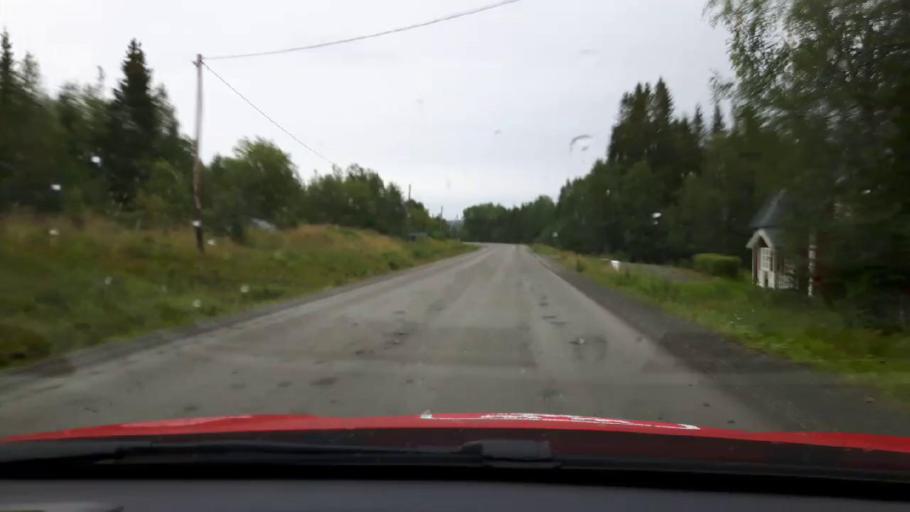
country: SE
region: Jaemtland
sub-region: Are Kommun
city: Are
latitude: 63.4558
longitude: 12.6442
